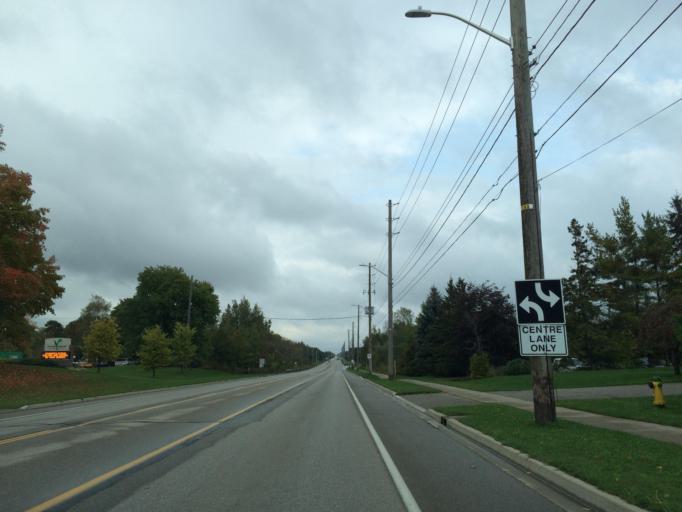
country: CA
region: Ontario
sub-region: Wellington County
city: Guelph
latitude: 43.5292
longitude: -80.1928
